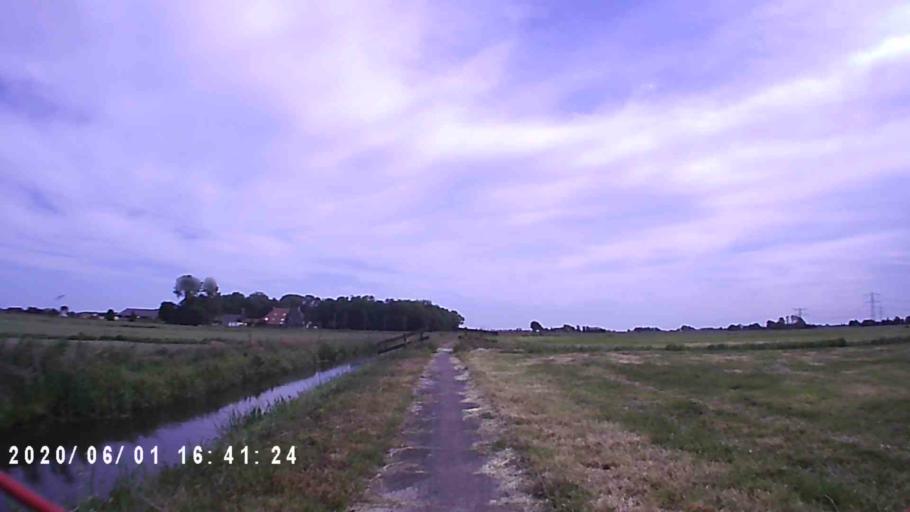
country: NL
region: Friesland
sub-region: Gemeente Boarnsterhim
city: Warten
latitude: 53.1844
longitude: 5.8778
